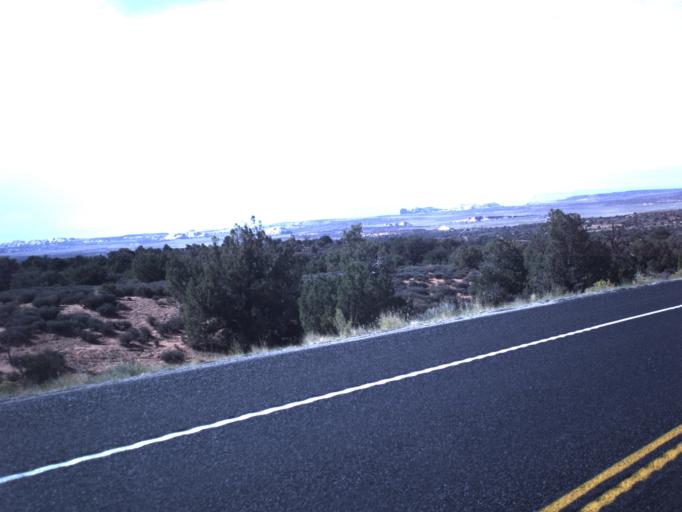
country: US
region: Utah
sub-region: Grand County
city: Moab
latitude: 38.6044
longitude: -109.8173
